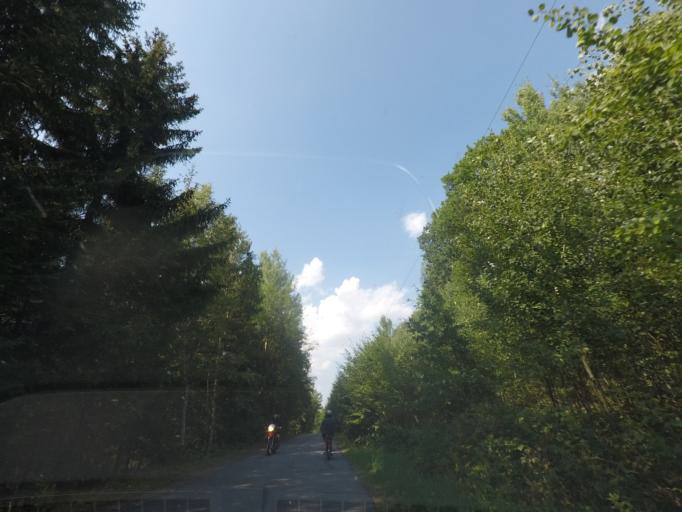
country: CZ
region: Pardubicky
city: Horni Jeleni
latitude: 50.0670
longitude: 16.0726
